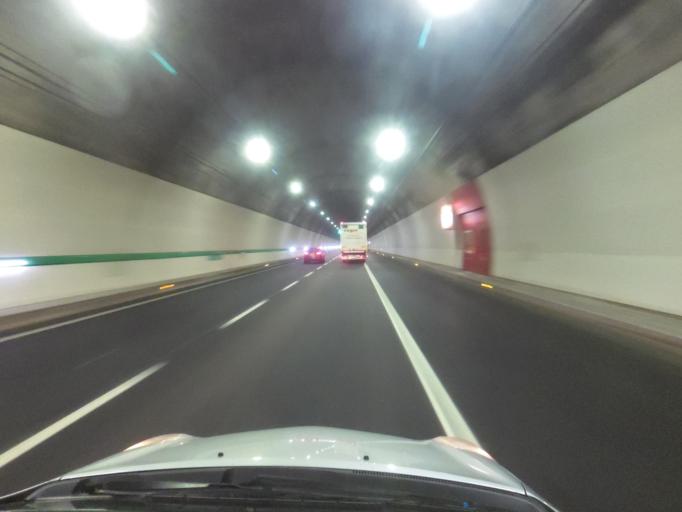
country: IT
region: Emilia-Romagna
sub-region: Provincia di Bologna
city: Castiglione dei Pepoli
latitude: 44.1387
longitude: 11.1914
